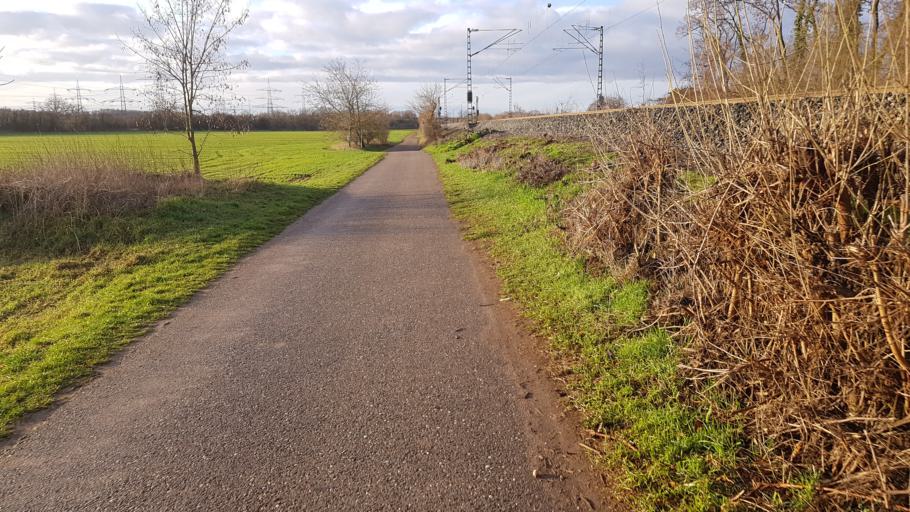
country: DE
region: Baden-Wuerttemberg
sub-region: Karlsruhe Region
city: Sandhausen
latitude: 49.3174
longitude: 8.6678
